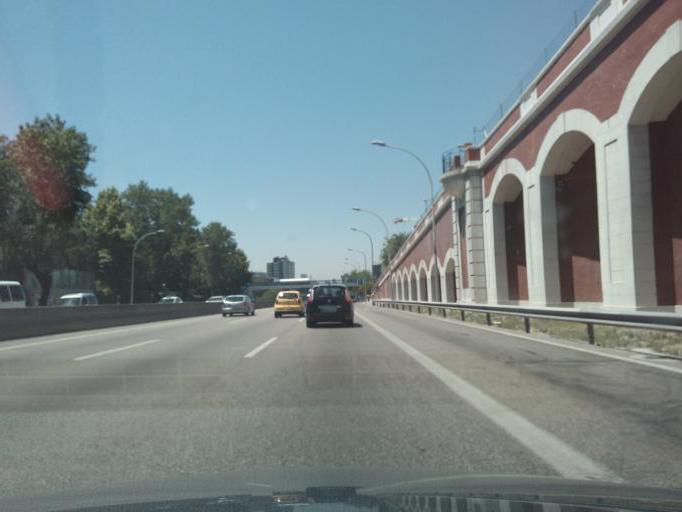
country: ES
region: Madrid
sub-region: Provincia de Madrid
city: Ciudad Lineal
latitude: 40.4485
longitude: -3.6508
